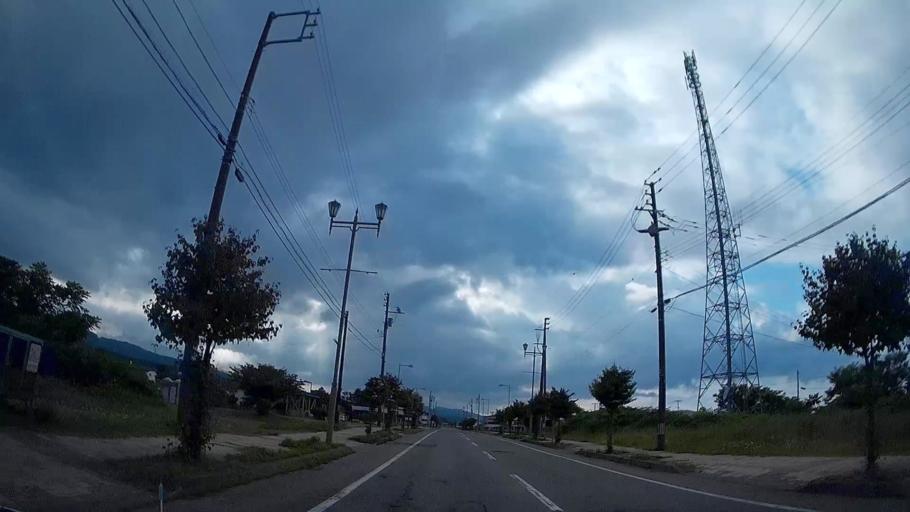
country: JP
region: Hokkaido
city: Nanae
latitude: 42.1092
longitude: 140.5696
